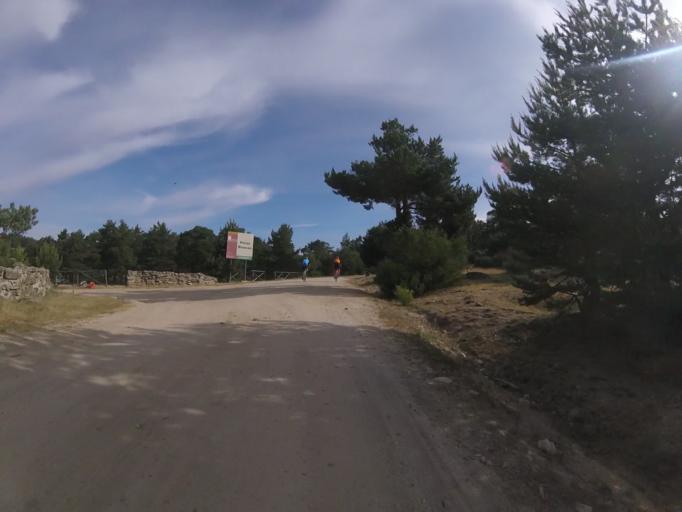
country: ES
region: Castille and Leon
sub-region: Provincia de Avila
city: Peguerinos
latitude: 40.6477
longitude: -4.1780
